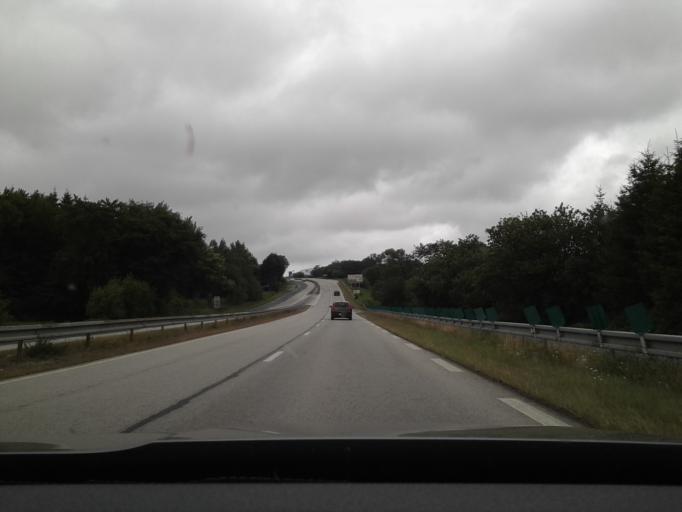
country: FR
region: Lower Normandy
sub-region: Departement de la Manche
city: La Glacerie
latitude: 49.5905
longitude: -1.5963
